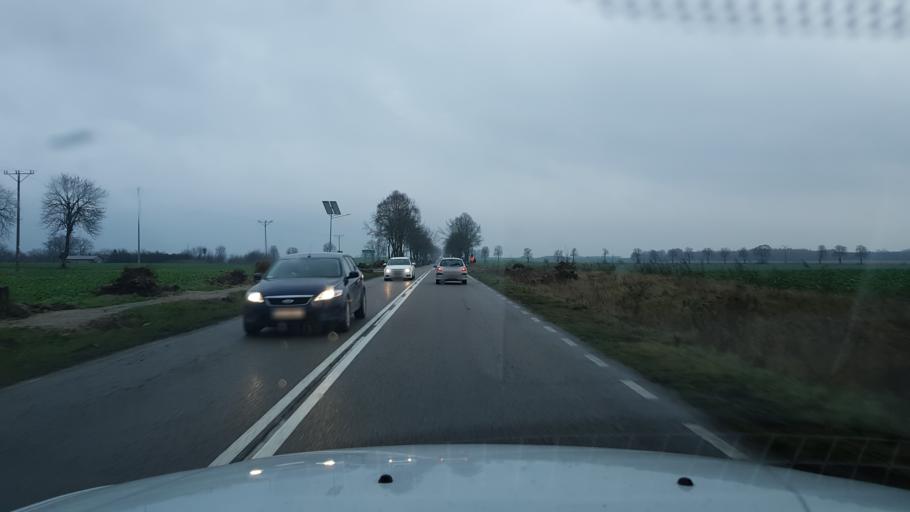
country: PL
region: West Pomeranian Voivodeship
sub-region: Powiat gryficki
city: Ploty
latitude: 53.8460
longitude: 15.2326
